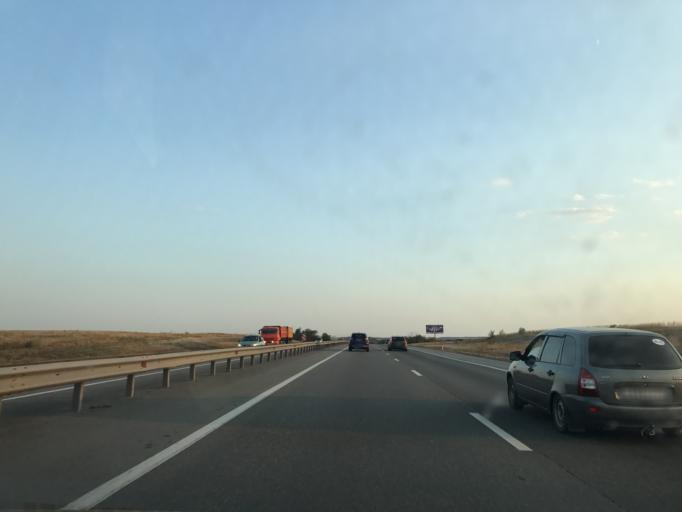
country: RU
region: Rostov
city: Likhoy
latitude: 48.0898
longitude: 40.2596
